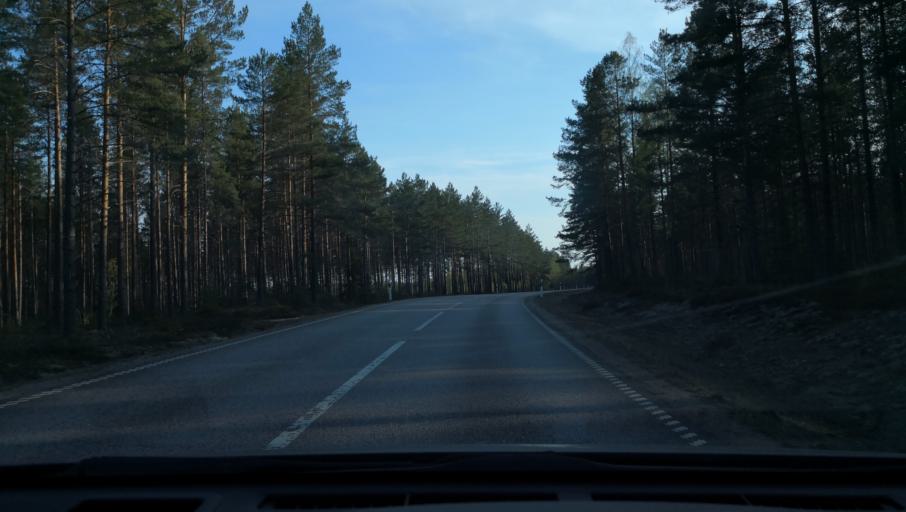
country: SE
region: Uppsala
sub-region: Heby Kommun
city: Heby
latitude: 60.0343
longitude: 16.8586
